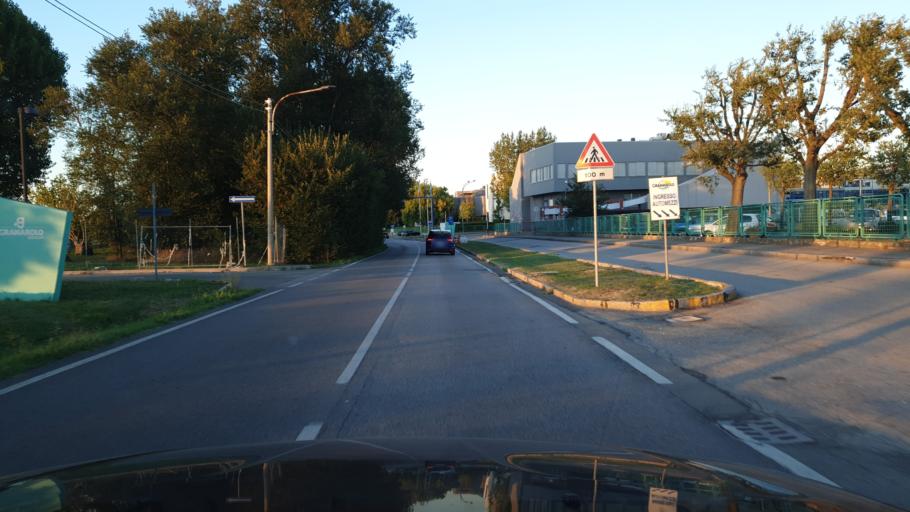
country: IT
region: Emilia-Romagna
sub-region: Provincia di Bologna
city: Quarto Inferiore
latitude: 44.5315
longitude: 11.3868
